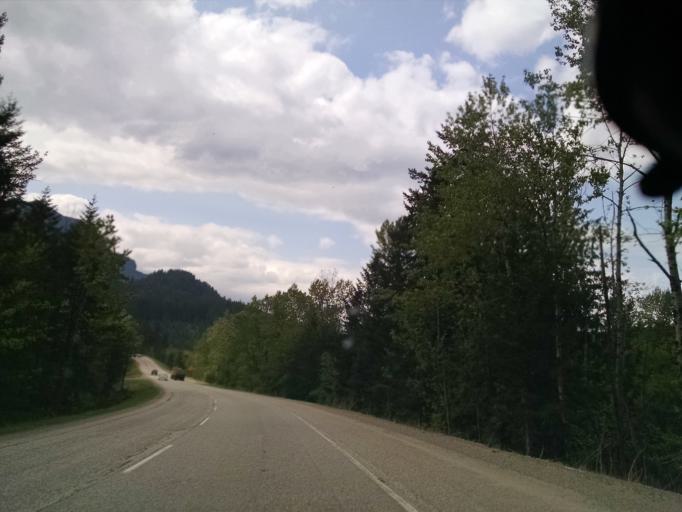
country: CA
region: British Columbia
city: Hope
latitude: 49.3796
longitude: -121.3556
